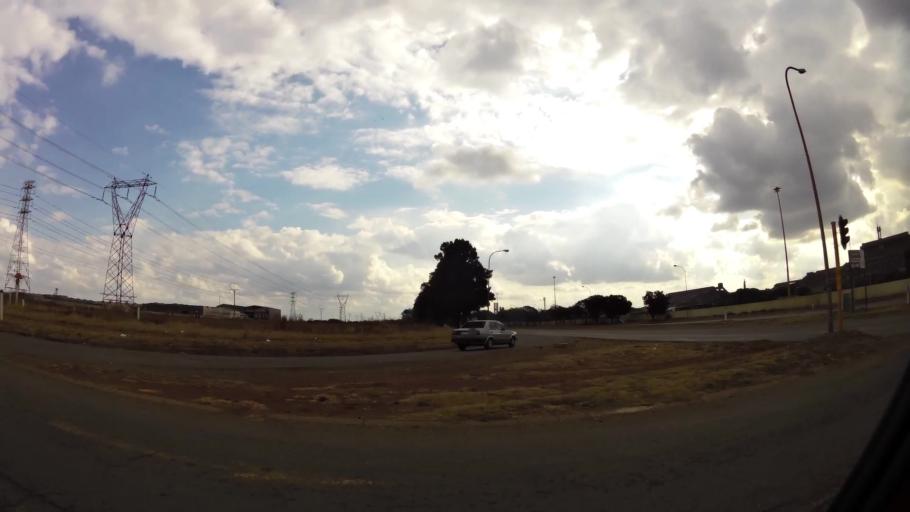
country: ZA
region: Gauteng
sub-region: Sedibeng District Municipality
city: Vanderbijlpark
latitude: -26.6730
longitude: 27.8183
